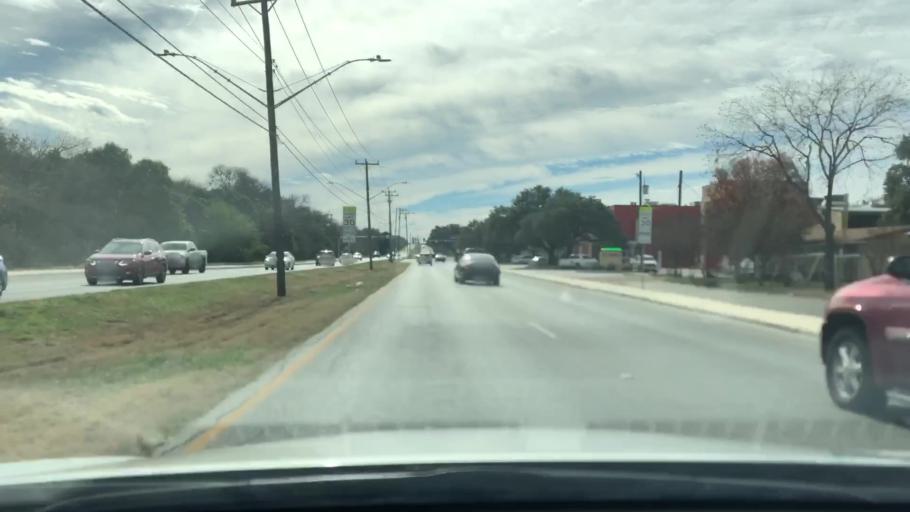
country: US
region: Texas
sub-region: Bexar County
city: Terrell Hills
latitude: 29.5076
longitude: -98.4346
